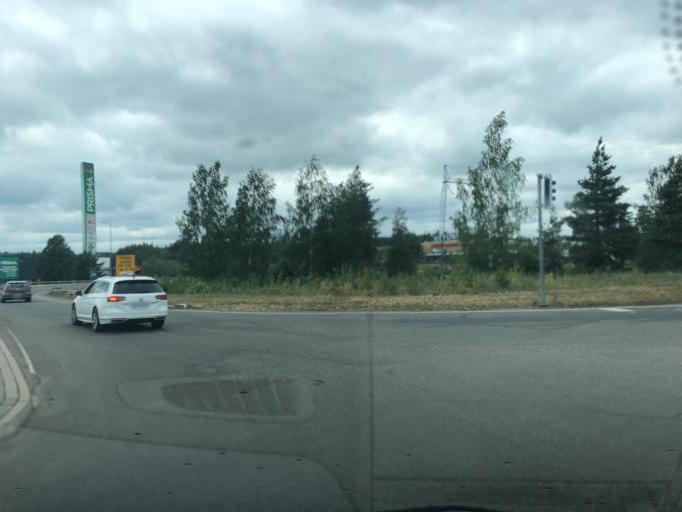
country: FI
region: Kymenlaakso
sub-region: Kouvola
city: Kouvola
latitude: 60.8733
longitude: 26.6589
